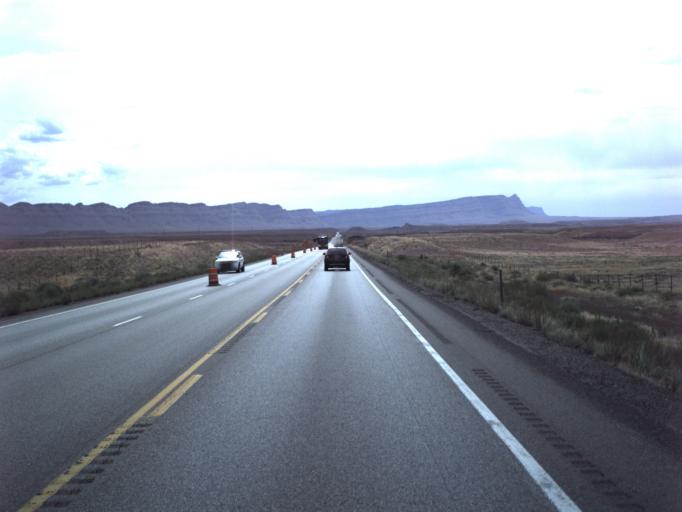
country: US
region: Utah
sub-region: Carbon County
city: East Carbon City
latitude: 39.3851
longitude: -110.4099
